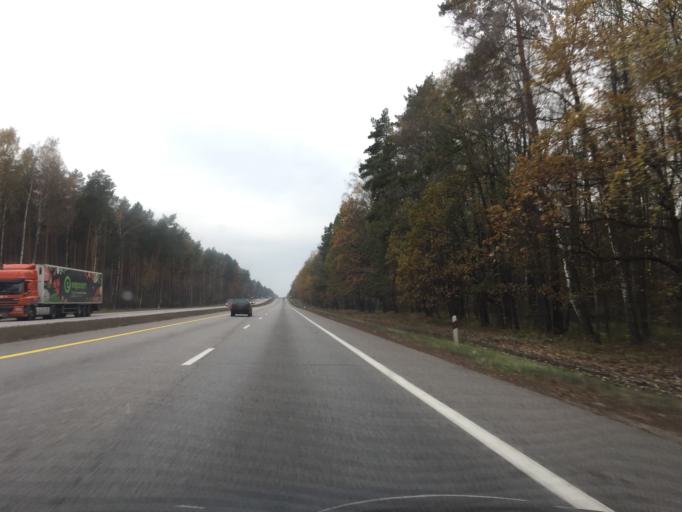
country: BY
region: Gomel
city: Gomel
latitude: 52.3818
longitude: 30.8018
